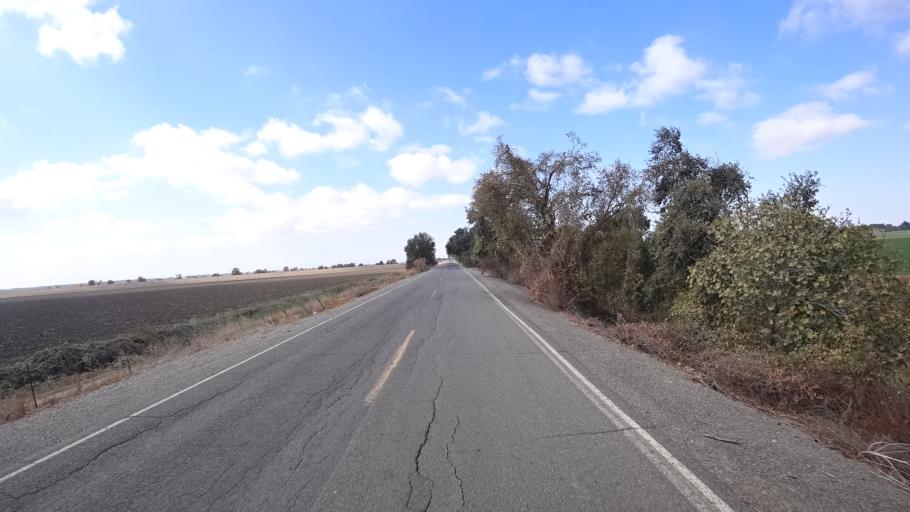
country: US
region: California
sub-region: Yolo County
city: Woodland
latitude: 38.7486
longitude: -121.6863
